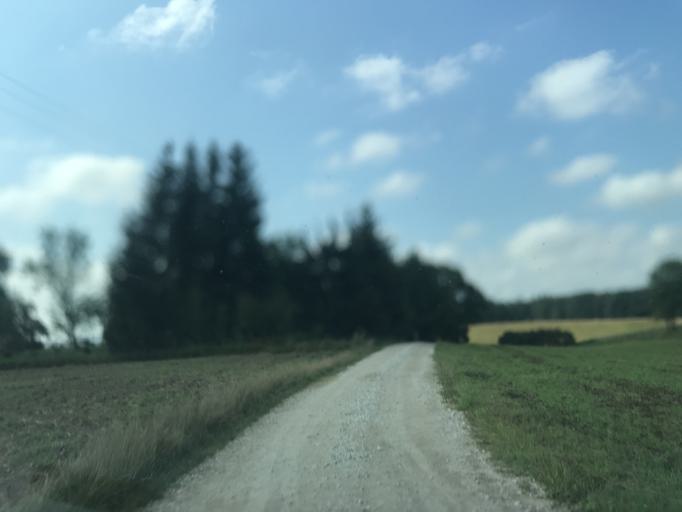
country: PL
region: Kujawsko-Pomorskie
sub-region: Powiat brodnicki
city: Brodnica
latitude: 53.3463
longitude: 19.4688
